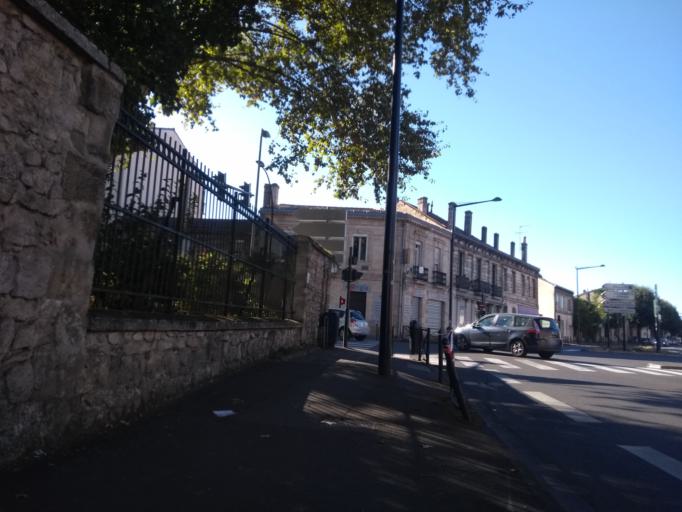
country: FR
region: Aquitaine
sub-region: Departement de la Gironde
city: Begles
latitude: 44.8146
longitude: -0.5723
